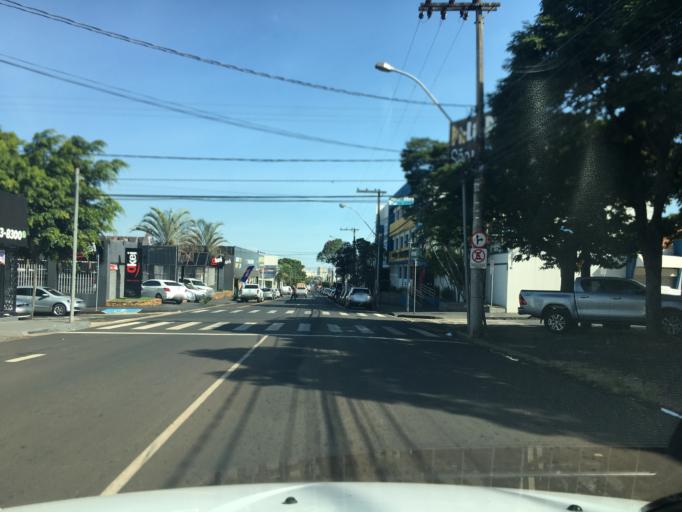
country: BR
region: Minas Gerais
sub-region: Uberlandia
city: Uberlandia
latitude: -18.8929
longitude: -48.2608
